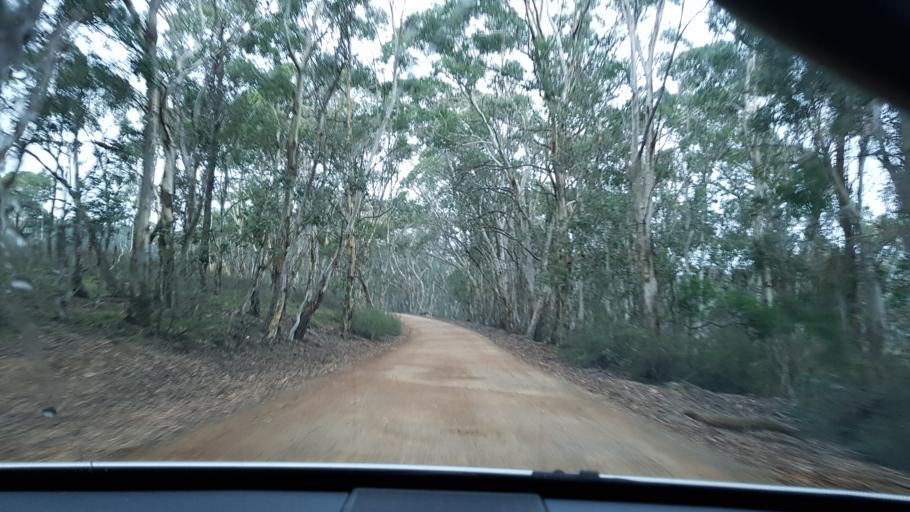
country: AU
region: New South Wales
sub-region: Oberon
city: Oberon
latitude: -33.9761
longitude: 150.0548
